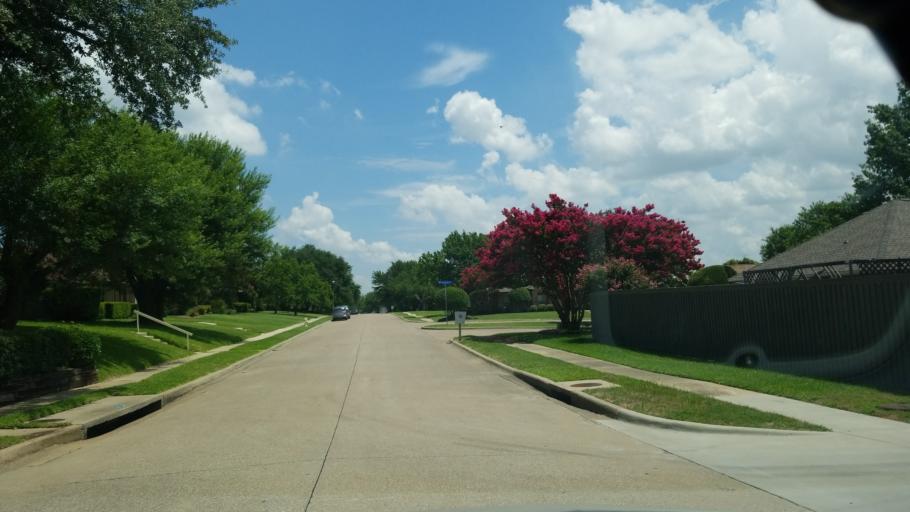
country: US
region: Texas
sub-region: Dallas County
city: Coppell
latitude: 32.9620
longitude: -96.9615
